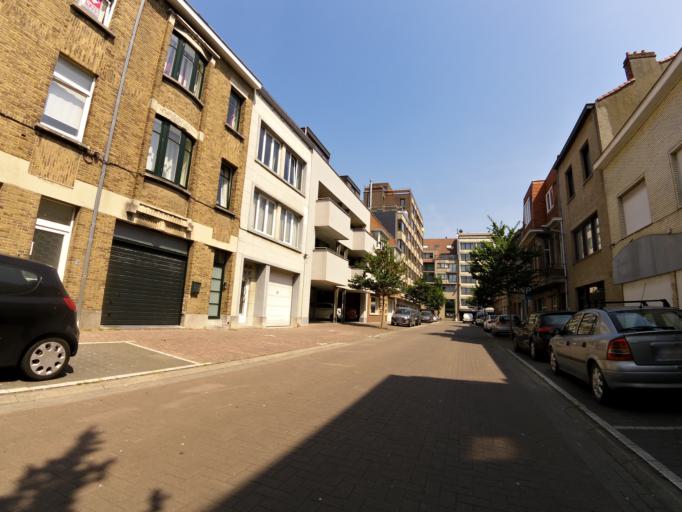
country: BE
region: Flanders
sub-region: Provincie West-Vlaanderen
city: Ostend
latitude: 51.2153
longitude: 2.9056
